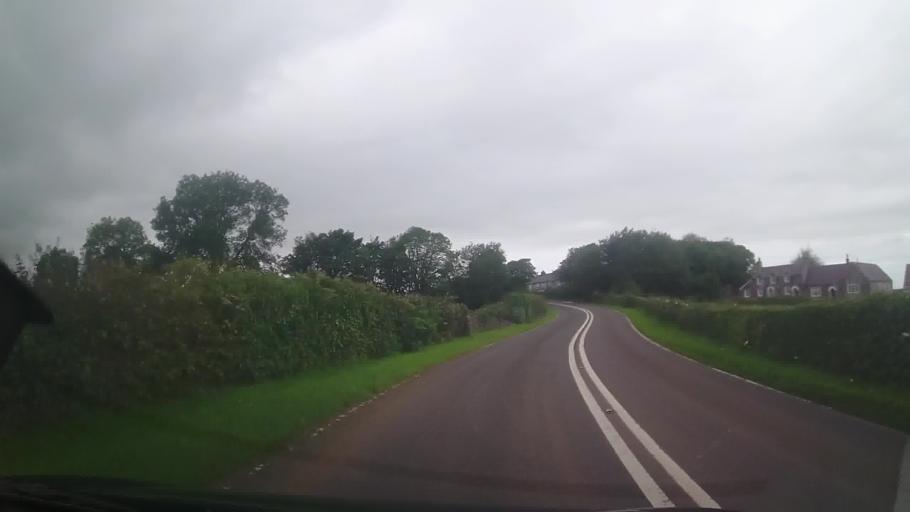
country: GB
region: Wales
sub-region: Anglesey
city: Gaerwen
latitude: 53.1817
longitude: -4.2627
